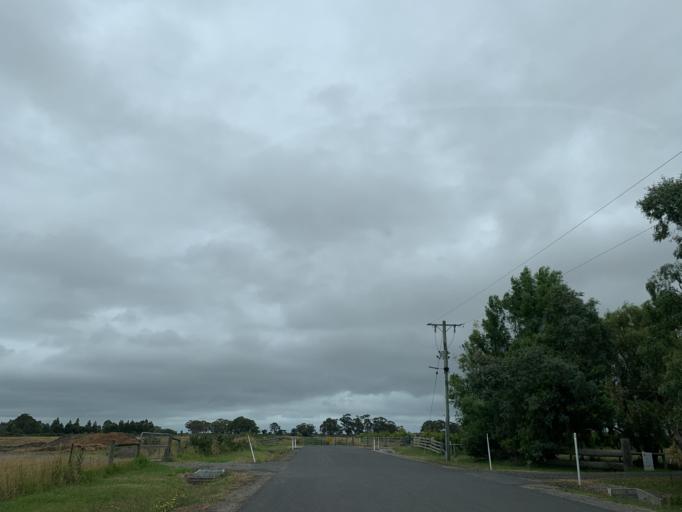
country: AU
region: Victoria
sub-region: Greater Dandenong
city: Keysborough
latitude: -38.0254
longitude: 145.1680
